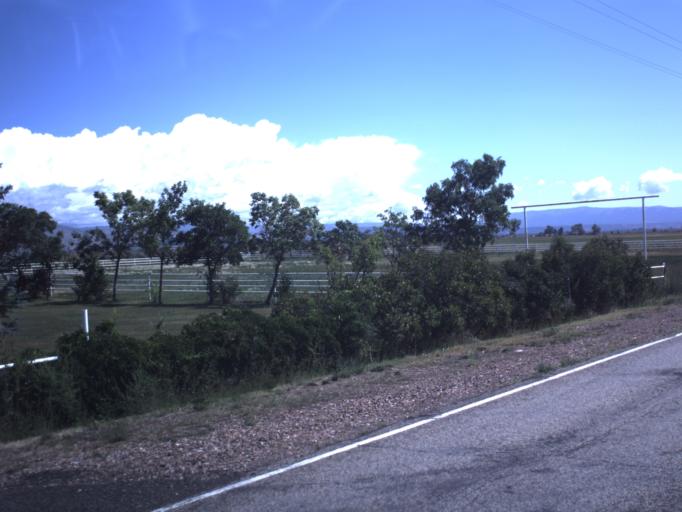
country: US
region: Utah
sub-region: Duchesne County
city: Roosevelt
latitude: 40.4329
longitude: -109.9937
